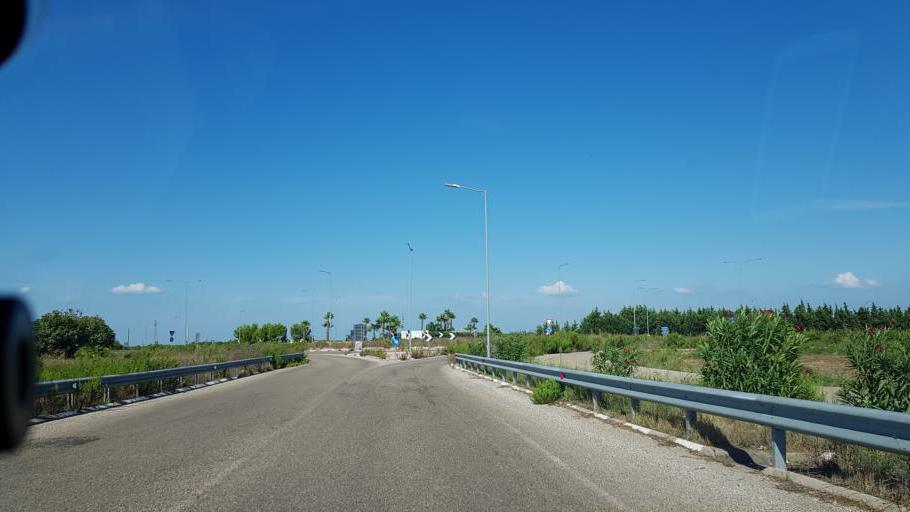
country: IT
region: Apulia
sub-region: Provincia di Lecce
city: Copertino
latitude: 40.2818
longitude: 18.0293
